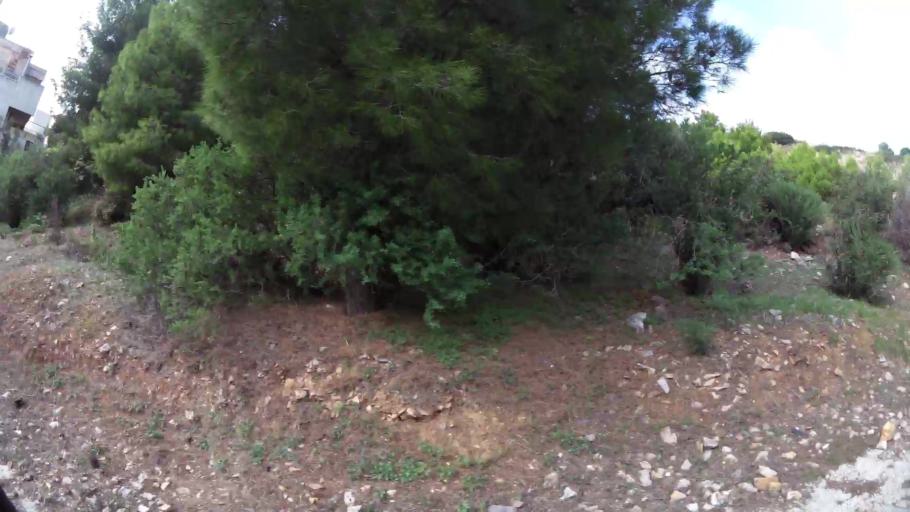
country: GR
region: Attica
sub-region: Nomarchia Athinas
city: Ymittos
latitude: 37.9486
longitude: 23.7628
